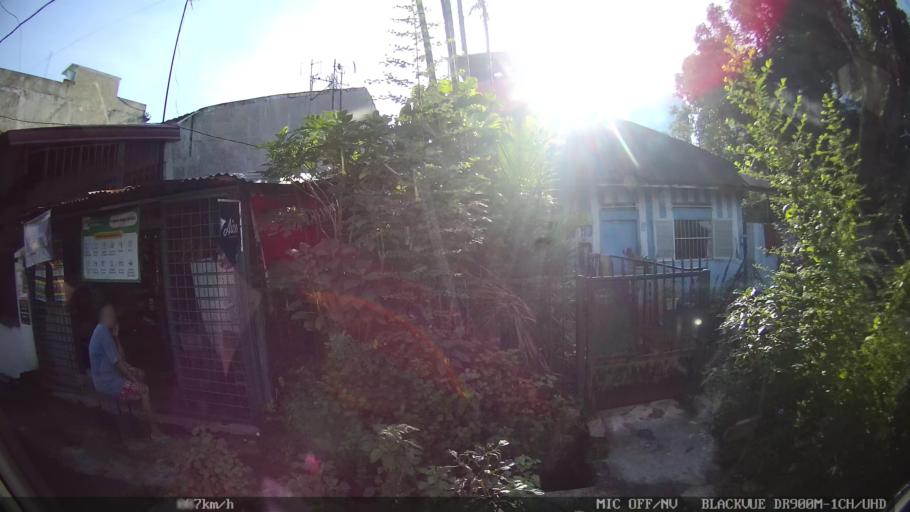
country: ID
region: North Sumatra
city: Medan
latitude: 3.5957
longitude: 98.6715
